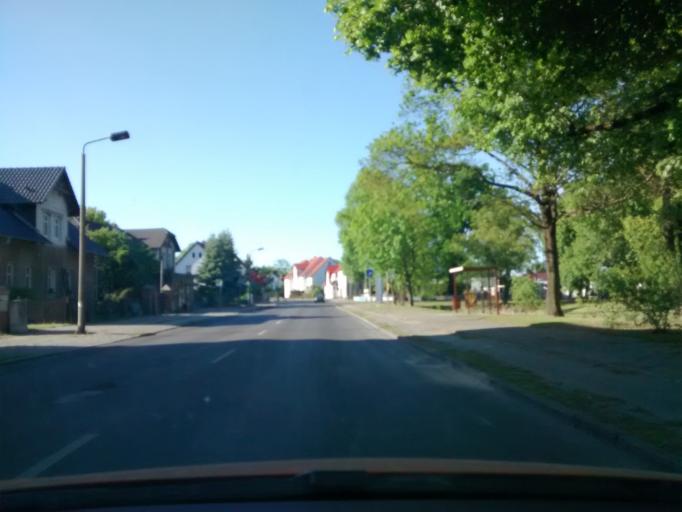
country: DE
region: Brandenburg
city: Furstenwalde
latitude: 52.3406
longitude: 14.0742
